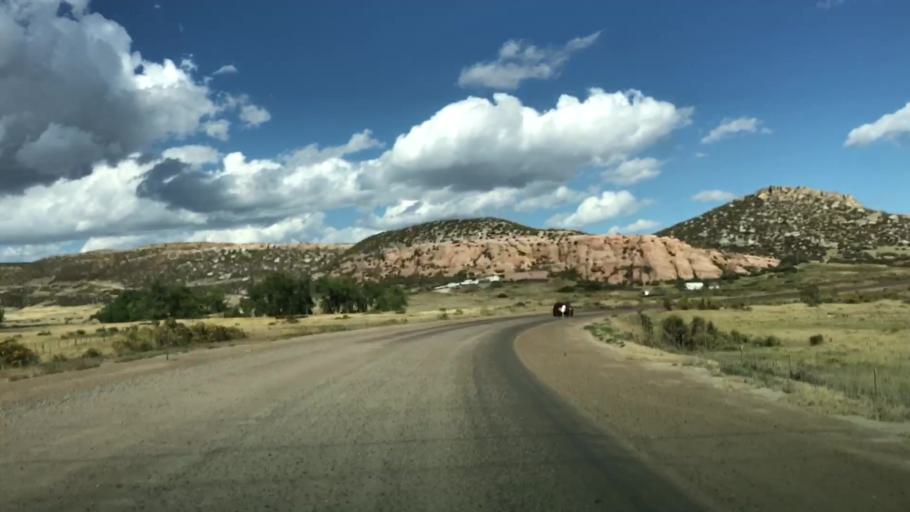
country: US
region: Colorado
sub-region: Larimer County
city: Laporte
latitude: 40.7800
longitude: -105.1520
